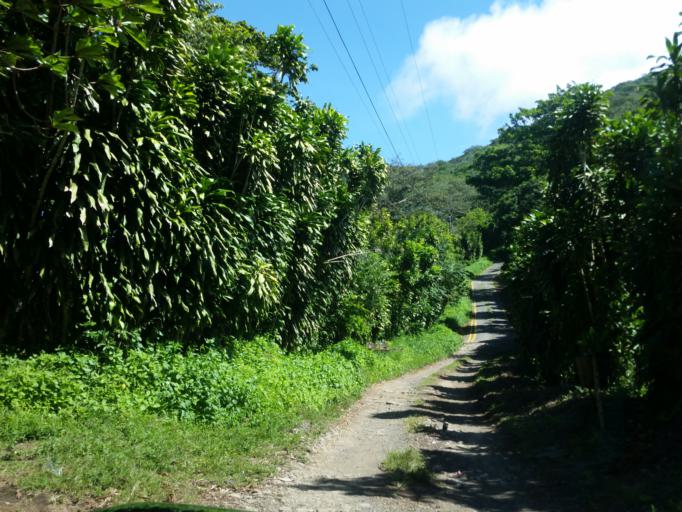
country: NI
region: Granada
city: Diriomo
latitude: 11.8386
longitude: -85.9885
